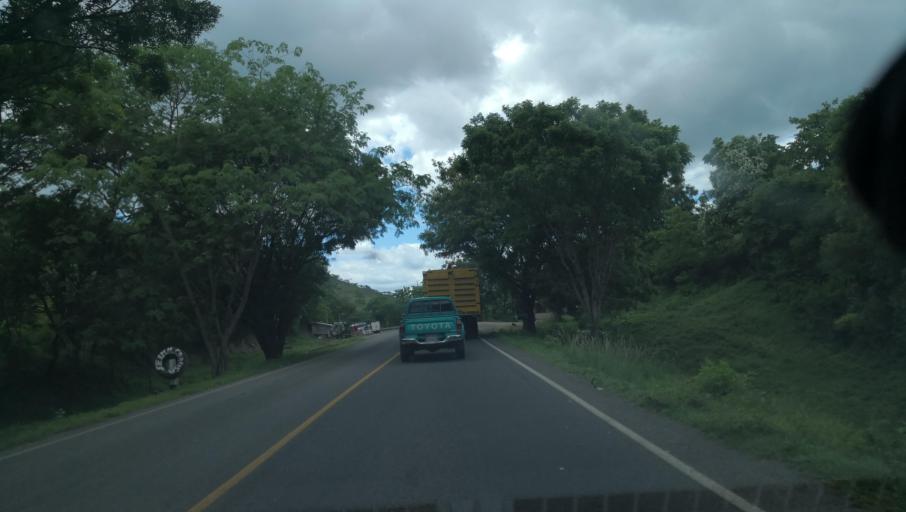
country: NI
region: Madriz
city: Yalaguina
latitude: 13.4580
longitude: -86.4606
